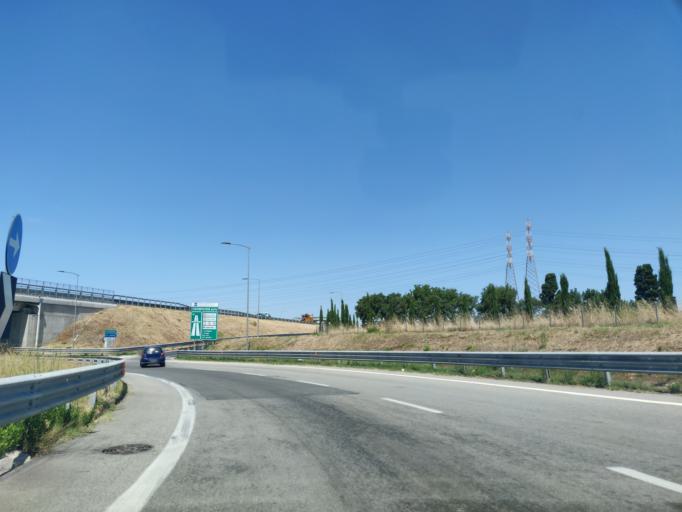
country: IT
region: Latium
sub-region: Citta metropolitana di Roma Capitale
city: Aurelia
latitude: 42.1643
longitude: 11.7897
